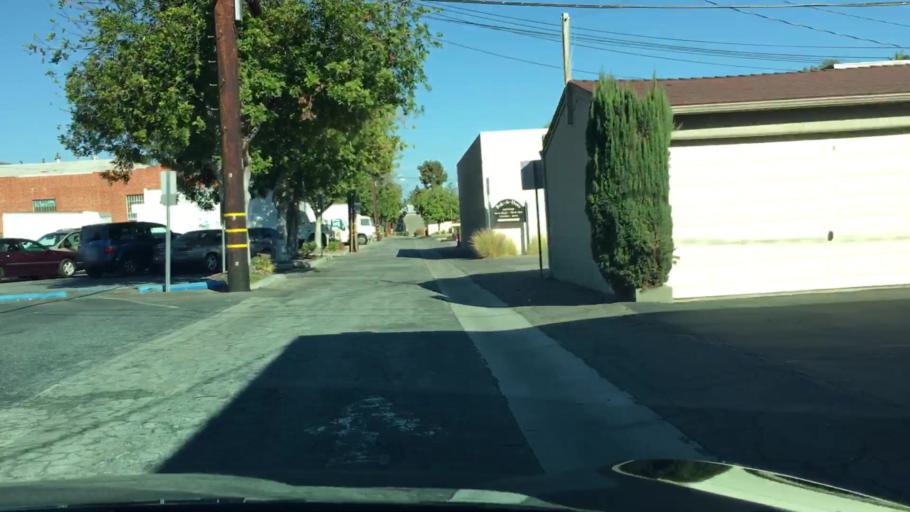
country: US
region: California
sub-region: Los Angeles County
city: Arcadia
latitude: 34.1407
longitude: -118.0280
